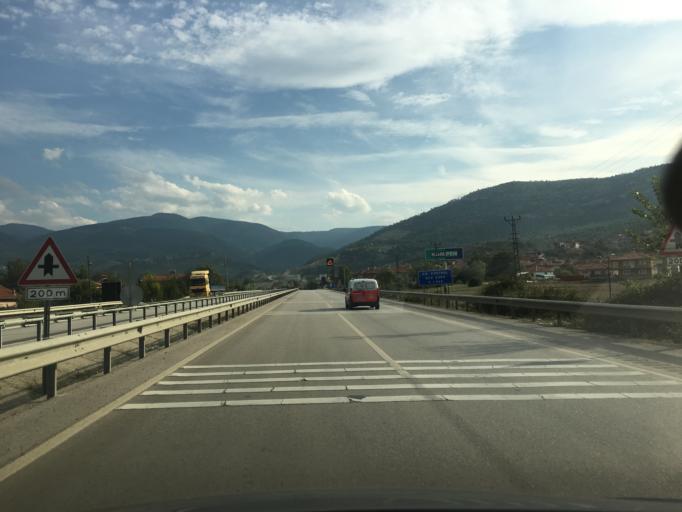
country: TR
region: Karabuk
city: Karabuk
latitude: 41.1071
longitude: 32.6684
